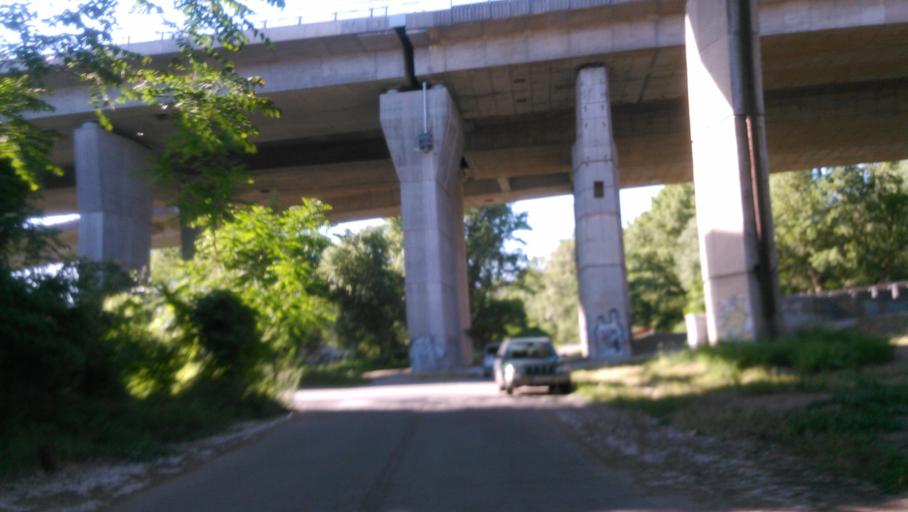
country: SK
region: Bratislavsky
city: Bratislava
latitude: 48.1309
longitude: 17.1347
